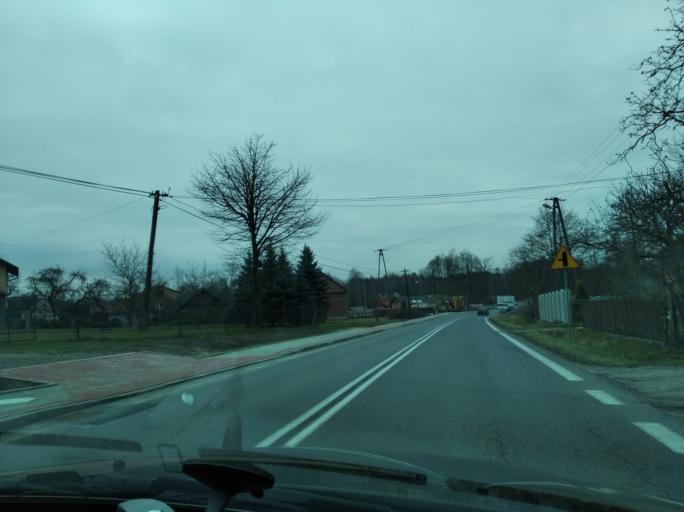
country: PL
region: Subcarpathian Voivodeship
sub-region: Powiat lancucki
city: Zolynia
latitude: 50.1494
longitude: 22.2749
